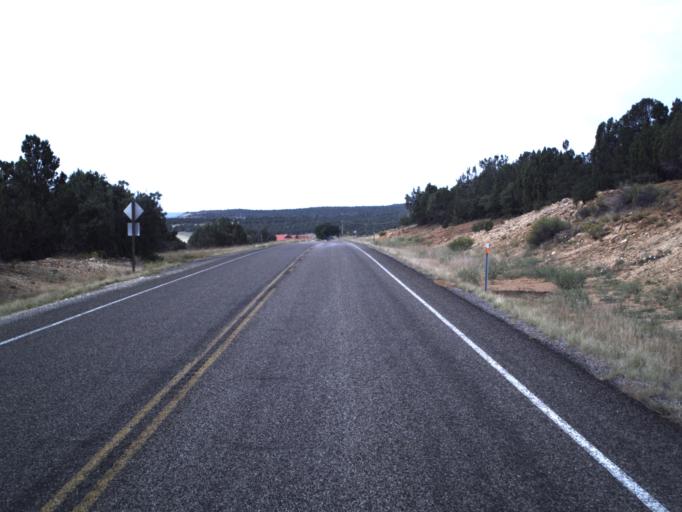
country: US
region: Utah
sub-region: Washington County
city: Hildale
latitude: 37.2509
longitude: -112.7989
